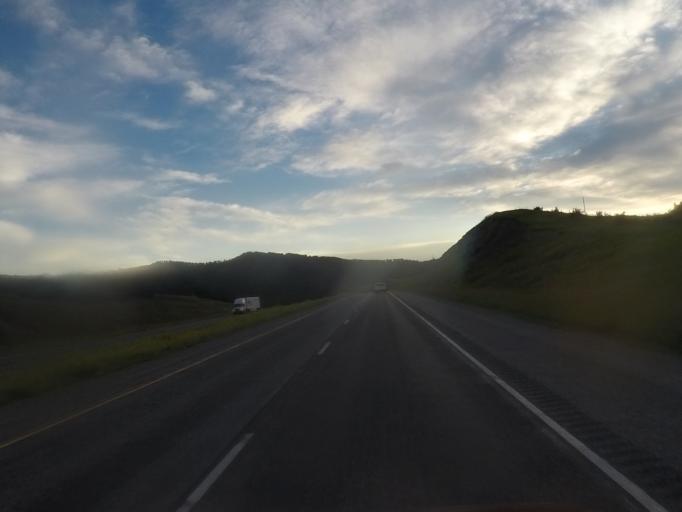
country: US
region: Montana
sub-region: Park County
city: Livingston
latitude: 45.6589
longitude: -110.7598
